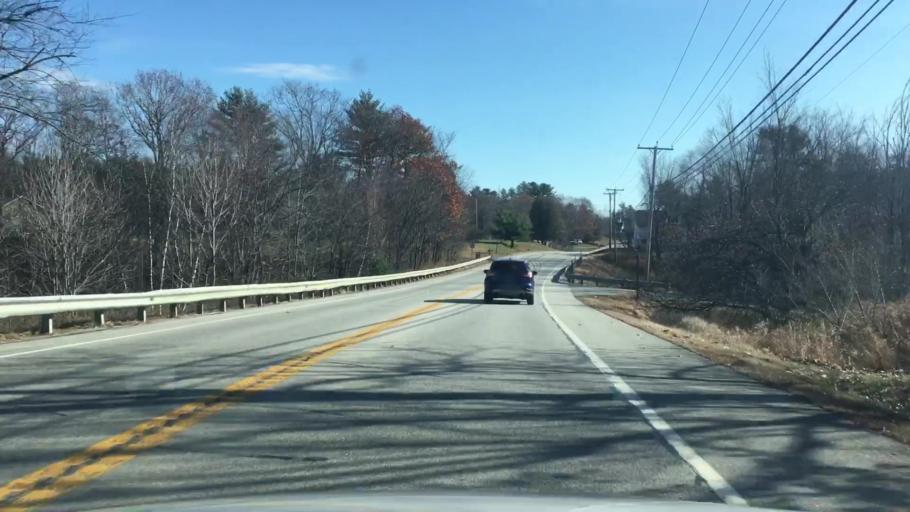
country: US
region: Maine
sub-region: Kennebec County
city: Chelsea
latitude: 44.2774
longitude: -69.6822
